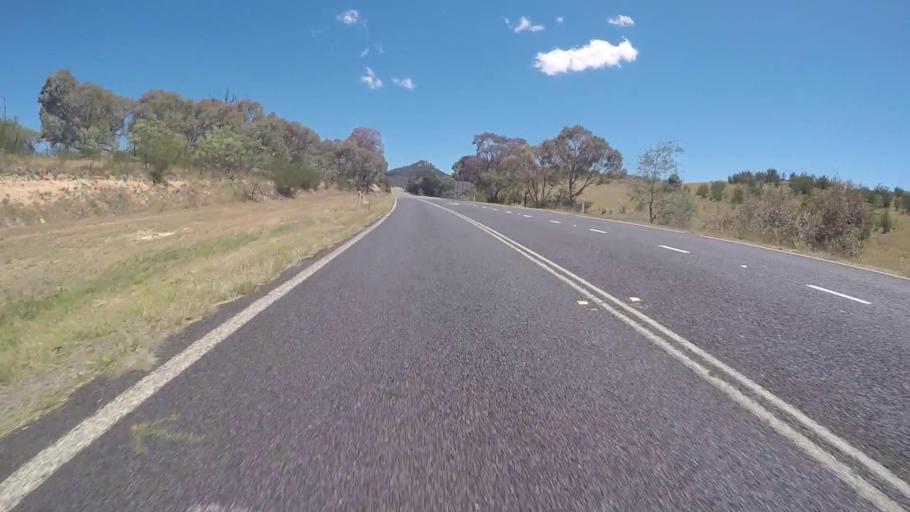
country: AU
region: Australian Capital Territory
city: Macarthur
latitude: -35.4501
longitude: 148.9750
